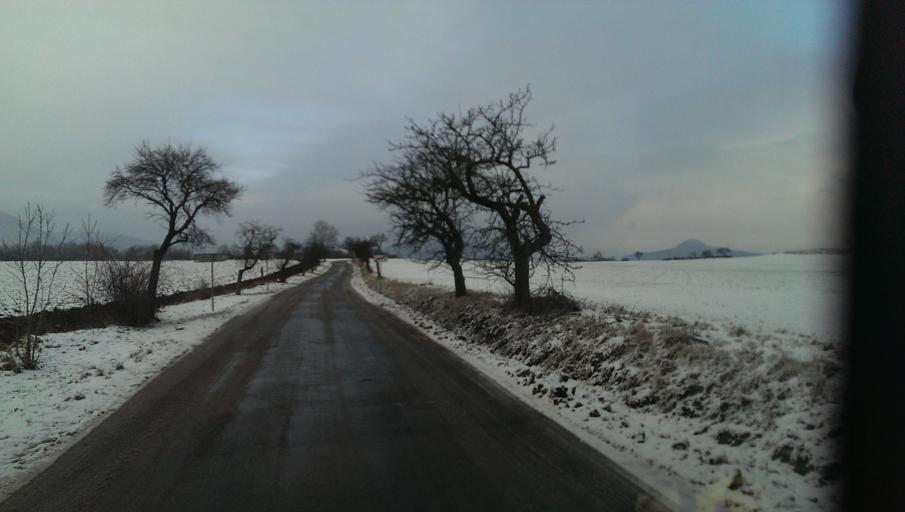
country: CZ
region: Ustecky
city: Trebenice
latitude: 50.4994
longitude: 13.9589
